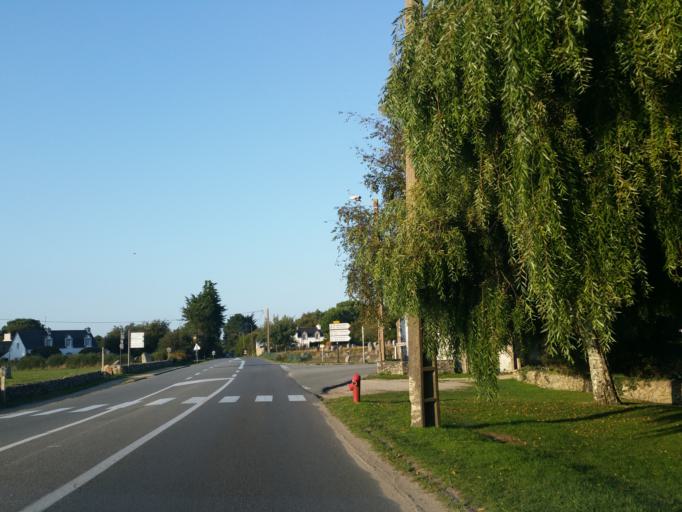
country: FR
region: Brittany
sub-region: Departement du Morbihan
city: Carnac
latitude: 47.5941
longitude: -3.0753
